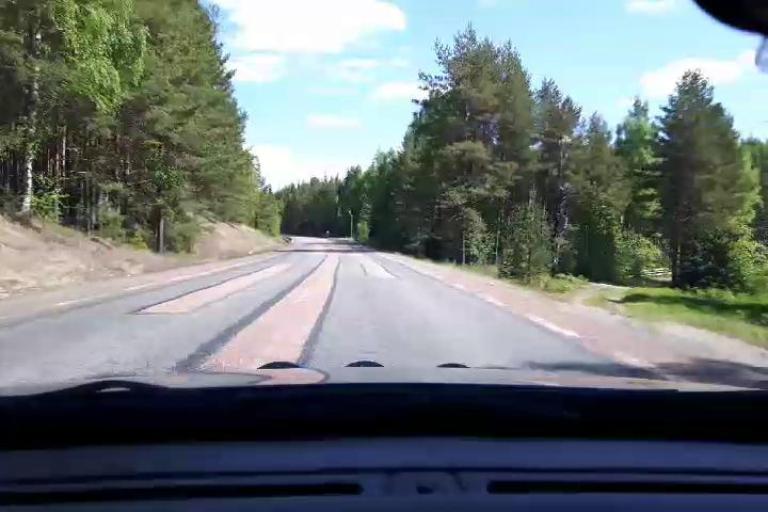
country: SE
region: Gaevleborg
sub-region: Ljusdals Kommun
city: Farila
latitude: 61.8884
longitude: 15.6749
